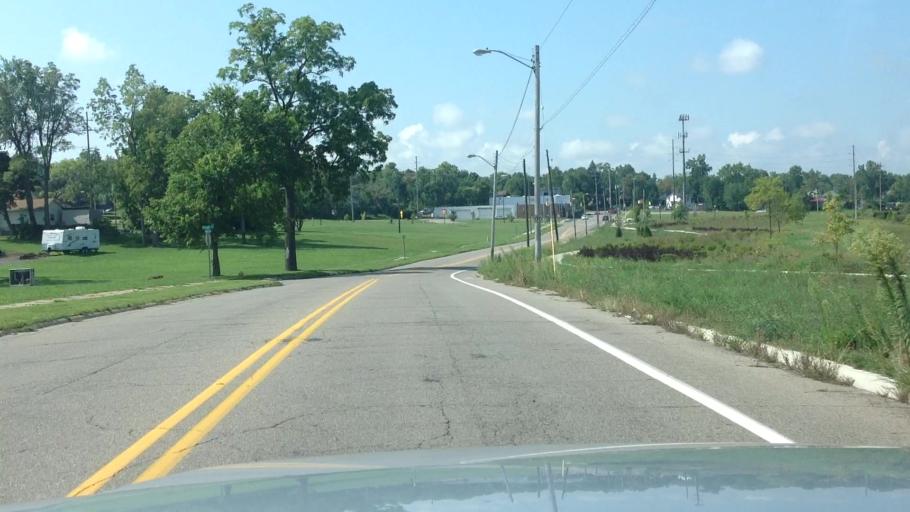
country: US
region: Michigan
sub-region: Genesee County
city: Flint
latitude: 43.0100
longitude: -83.7043
